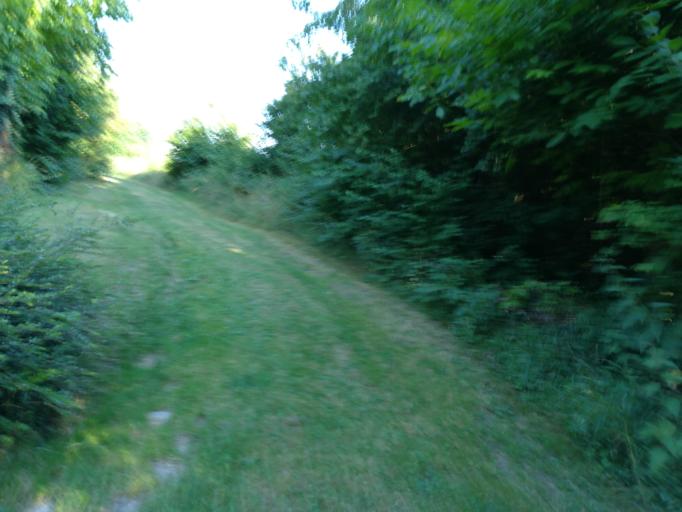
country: DE
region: Baden-Wuerttemberg
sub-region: Freiburg Region
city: Singen
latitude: 47.7533
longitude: 8.8222
